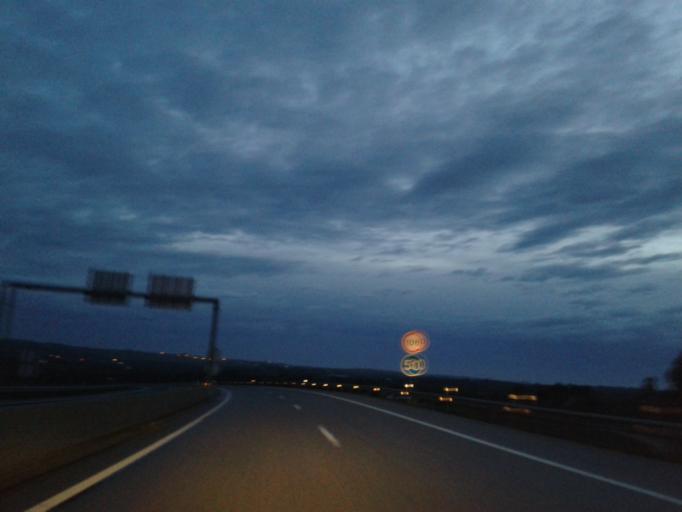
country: PT
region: Faro
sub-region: Lagos
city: Lagos
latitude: 37.1398
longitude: -8.7200
